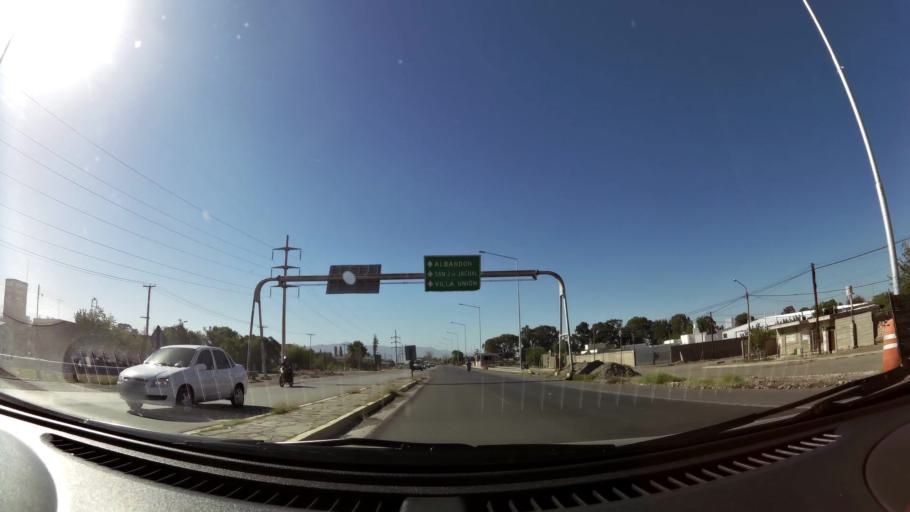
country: AR
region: San Juan
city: Villa Paula de Sarmiento
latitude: -31.5008
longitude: -68.5178
